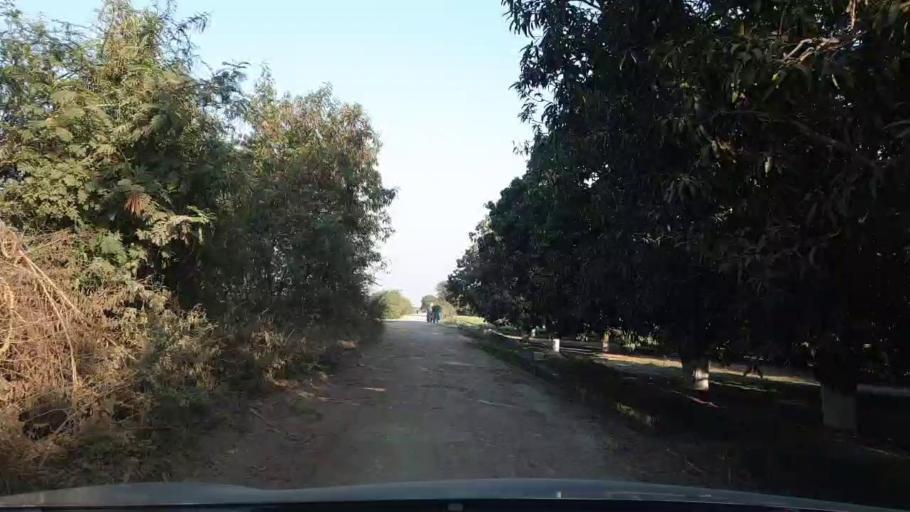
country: PK
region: Sindh
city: Tando Allahyar
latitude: 25.5732
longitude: 68.7749
